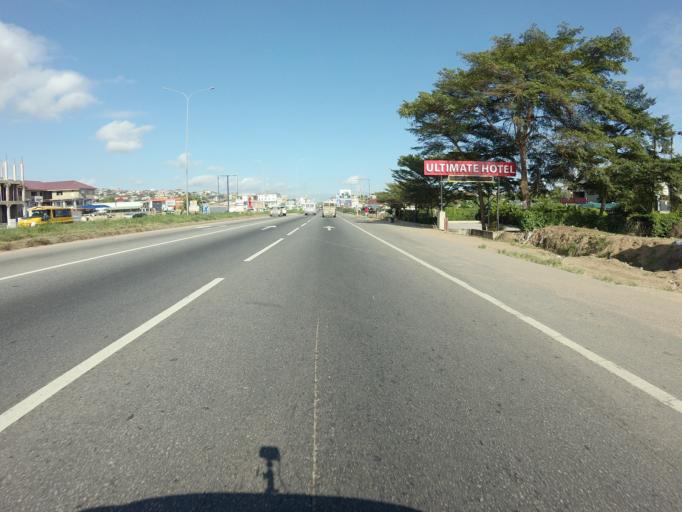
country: GH
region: Greater Accra
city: Gbawe
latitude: 5.5484
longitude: -0.3497
